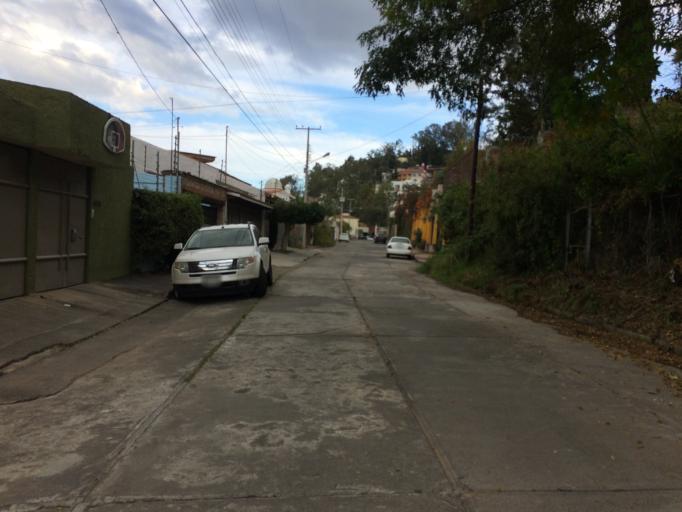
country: MX
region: Michoacan
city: Morelia
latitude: 19.6793
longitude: -101.1903
